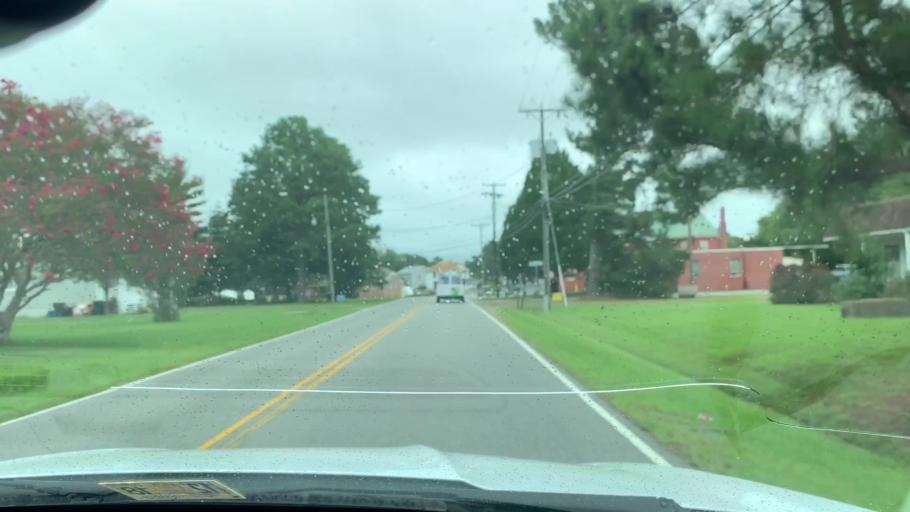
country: US
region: Virginia
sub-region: Gloucester County
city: Gloucester Point
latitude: 37.1951
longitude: -76.4328
